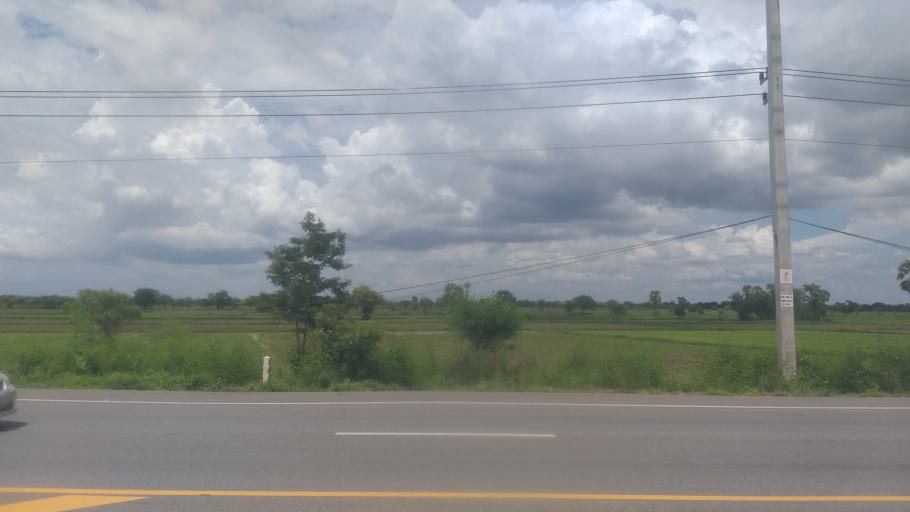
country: TH
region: Nakhon Ratchasima
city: Non Thai
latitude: 15.1242
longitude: 102.1030
